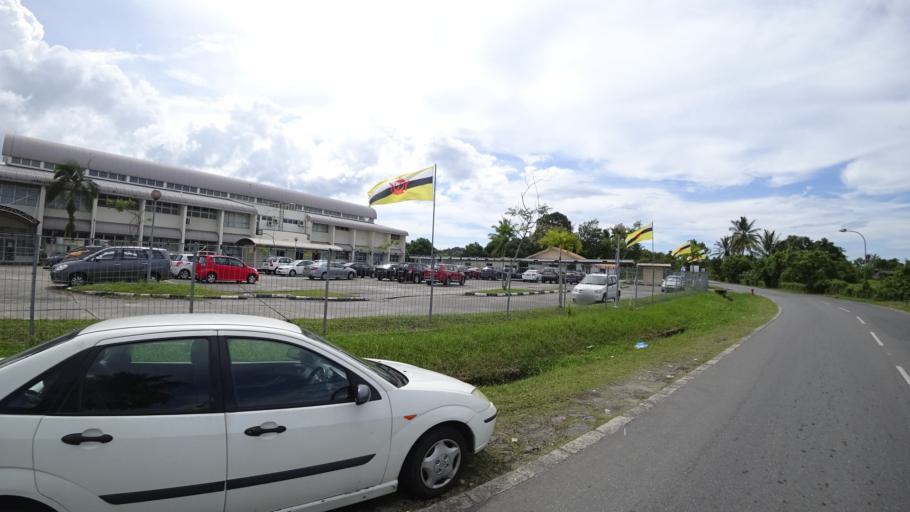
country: BN
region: Brunei and Muara
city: Bandar Seri Begawan
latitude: 4.8916
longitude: 114.8459
